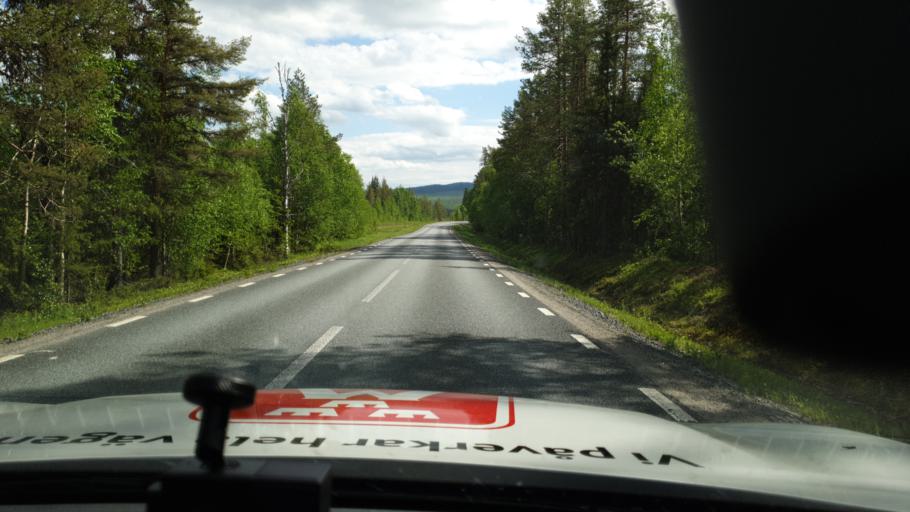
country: SE
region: Vaesterbotten
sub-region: Sorsele Kommun
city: Sorsele
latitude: 65.4515
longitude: 17.5755
